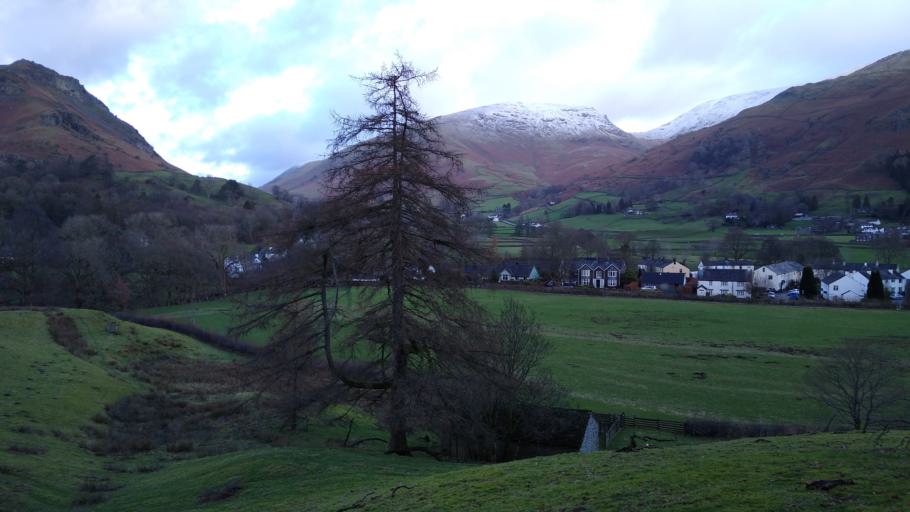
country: GB
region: England
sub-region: Cumbria
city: Ambleside
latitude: 54.4613
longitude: -3.0301
